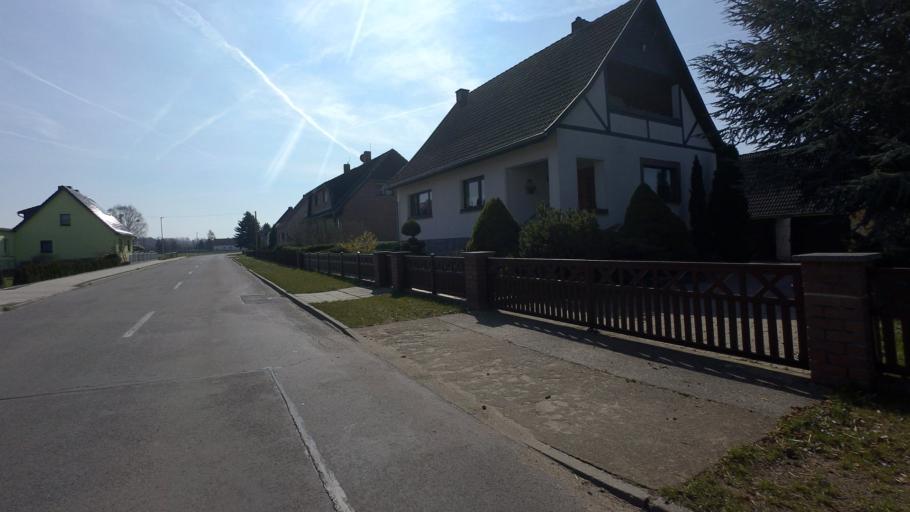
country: DE
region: Brandenburg
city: Drahnsdorf
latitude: 51.9347
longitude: 13.5946
